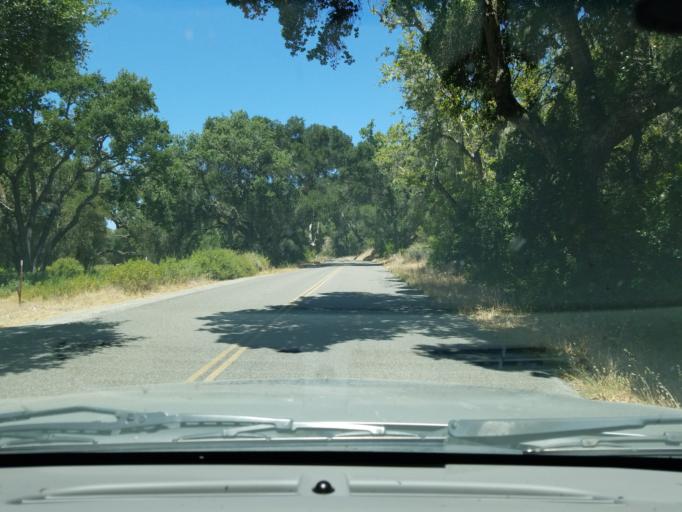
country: US
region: California
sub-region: Monterey County
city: Chualar
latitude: 36.4166
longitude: -121.6051
